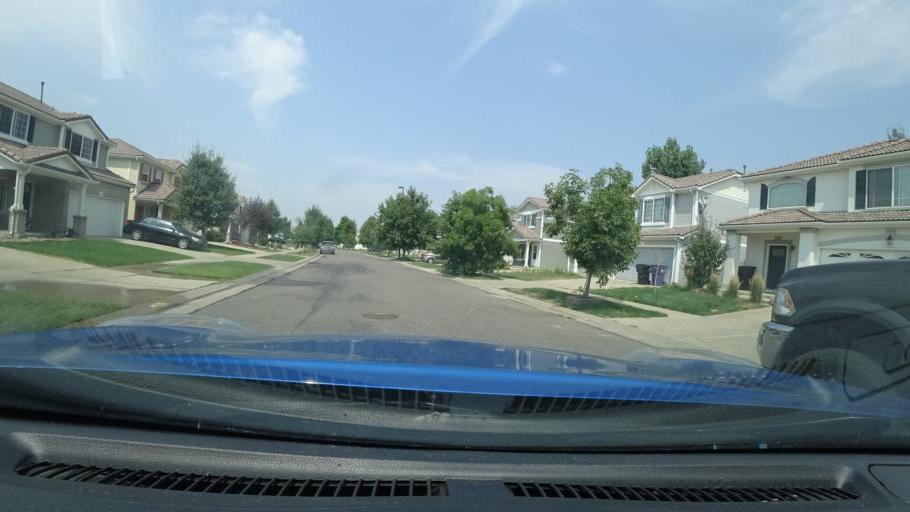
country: US
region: Colorado
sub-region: Adams County
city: Aurora
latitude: 39.7831
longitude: -104.7579
